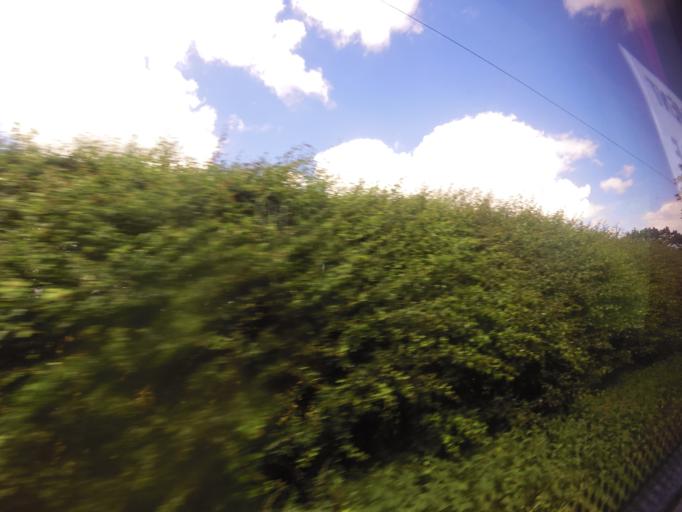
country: GB
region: England
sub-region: Norfolk
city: Aylsham
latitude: 52.8459
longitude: 1.2786
